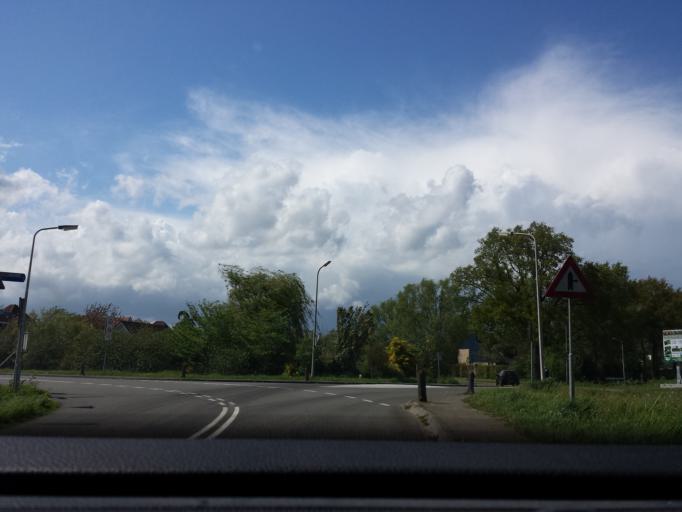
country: NL
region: Gelderland
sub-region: Gemeente Lochem
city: Barchem
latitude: 52.0903
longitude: 6.4604
